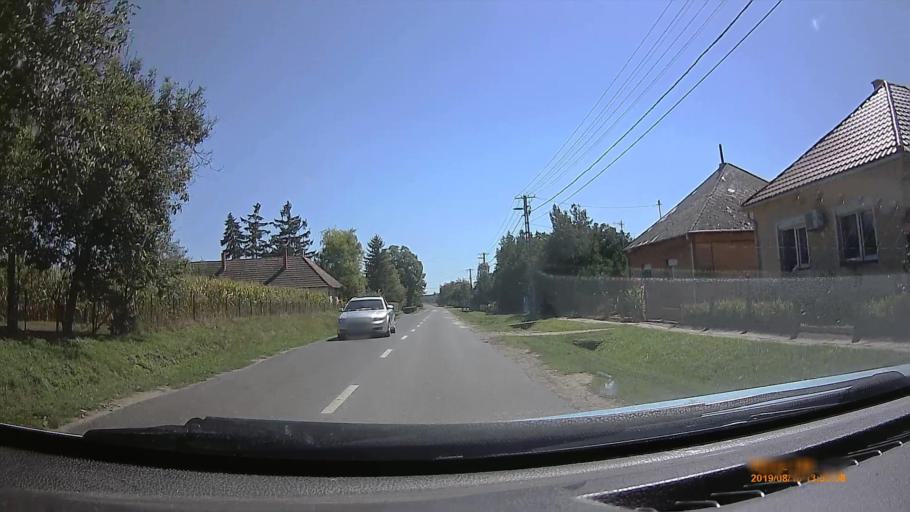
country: HU
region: Fejer
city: Cece
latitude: 46.7808
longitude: 18.5970
